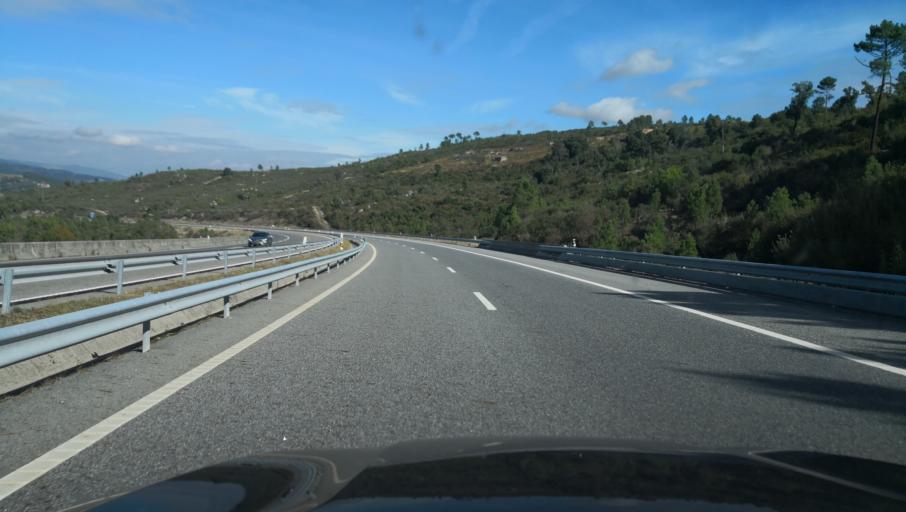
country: PT
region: Vila Real
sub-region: Boticas
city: Boticas
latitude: 41.6234
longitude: -7.5986
